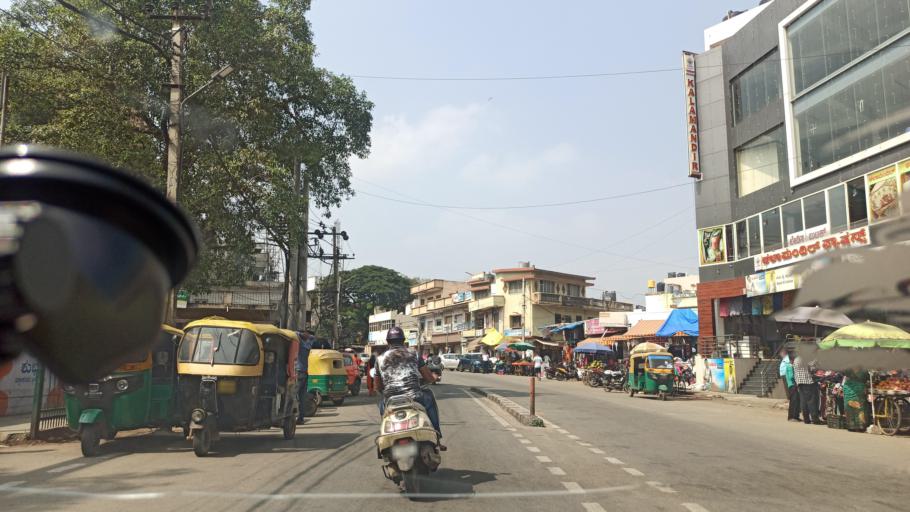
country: IN
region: Karnataka
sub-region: Bangalore Urban
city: Yelahanka
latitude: 13.0998
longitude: 77.5965
